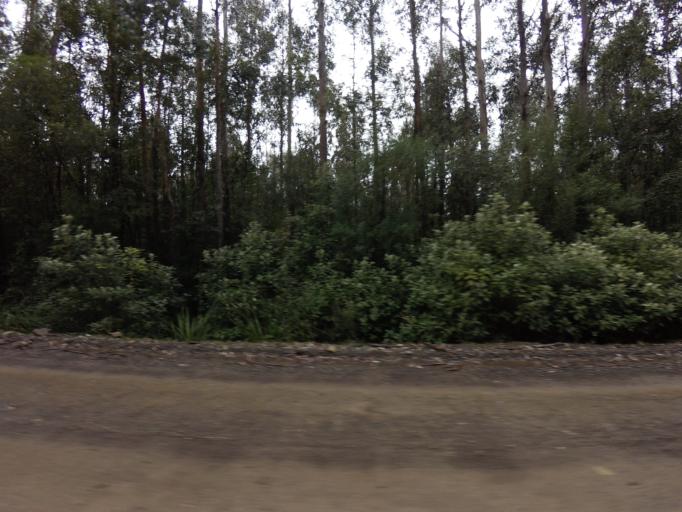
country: AU
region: Tasmania
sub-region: Huon Valley
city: Geeveston
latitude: -43.4750
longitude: 146.8921
